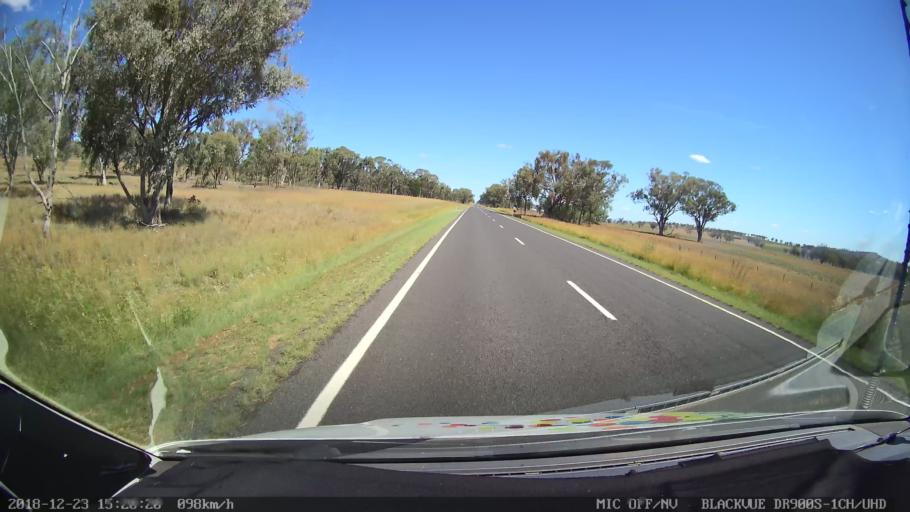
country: AU
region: New South Wales
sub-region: Tamworth Municipality
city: Manilla
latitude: -30.8413
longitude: 150.7890
